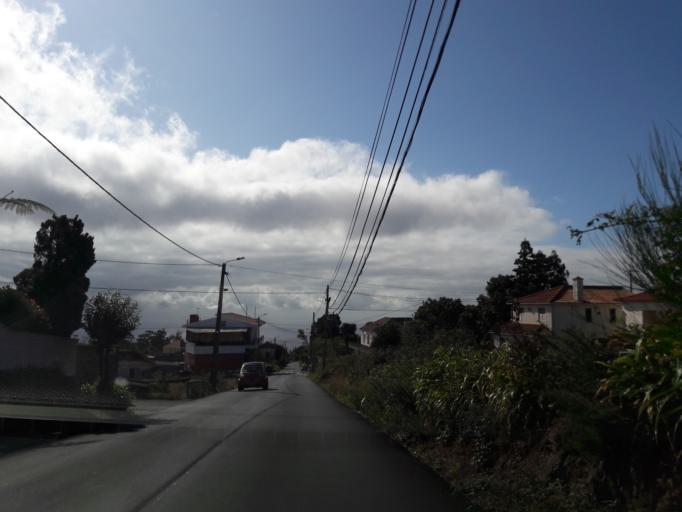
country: PT
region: Madeira
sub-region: Santa Cruz
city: Camacha
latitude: 32.6692
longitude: -16.8433
